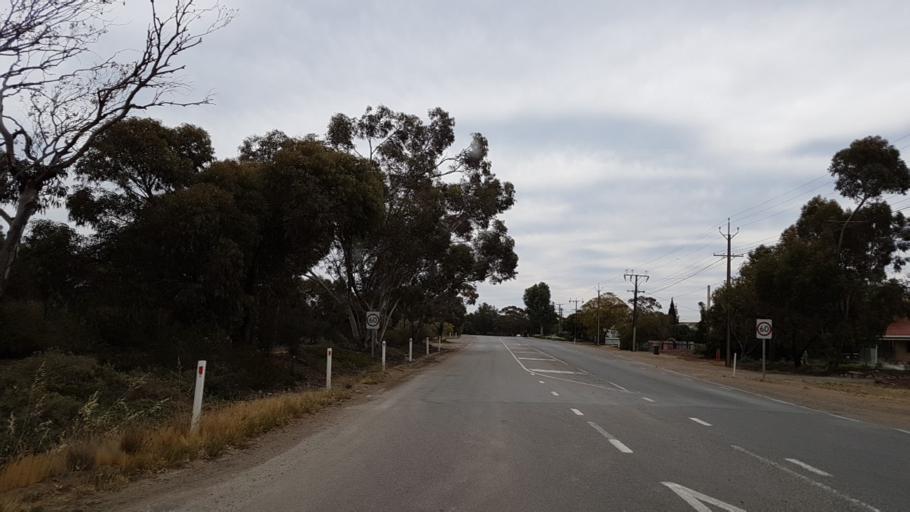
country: AU
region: South Australia
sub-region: Port Pirie City and Dists
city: Solomontown
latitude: -33.1885
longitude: 138.0317
